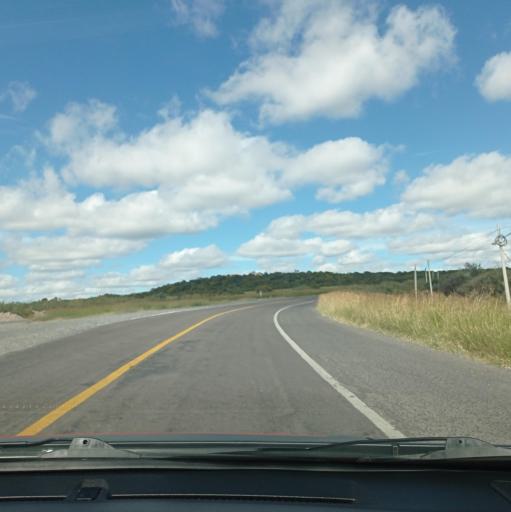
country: MX
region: Jalisco
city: San Diego de Alejandria
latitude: 20.9995
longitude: -102.0055
